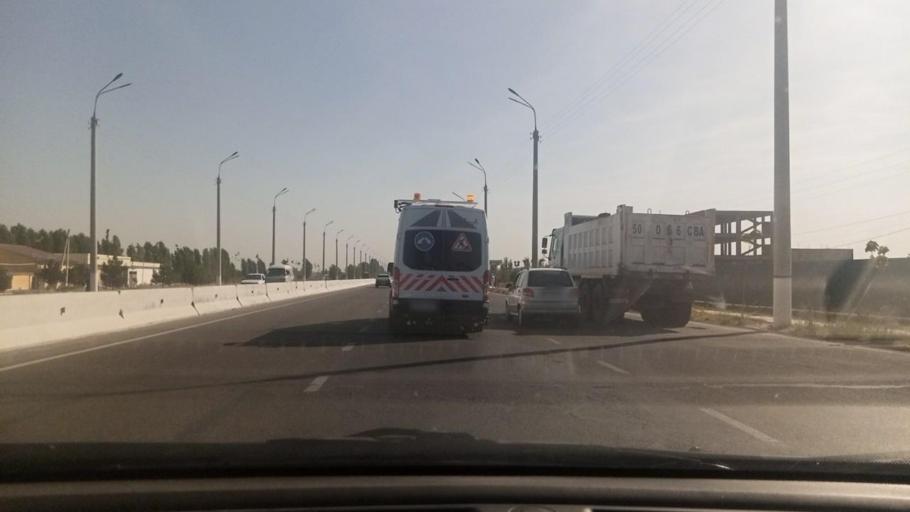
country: UZ
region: Toshkent Shahri
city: Bektemir
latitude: 41.2051
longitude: 69.3366
